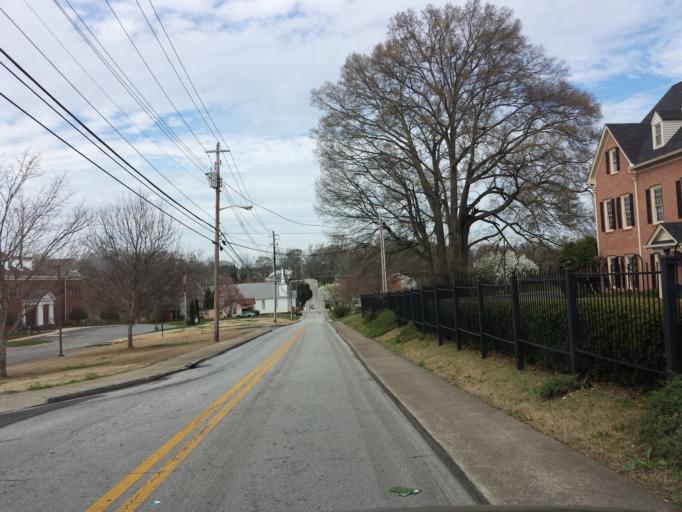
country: US
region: Georgia
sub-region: Cobb County
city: Marietta
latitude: 33.9532
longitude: -84.5435
